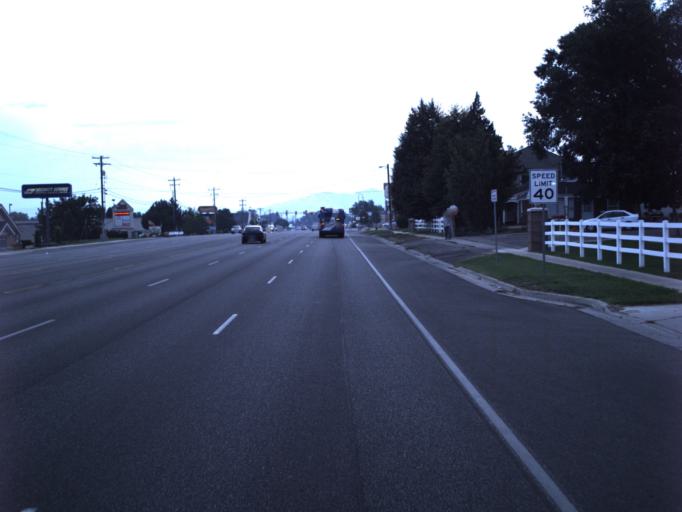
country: US
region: Utah
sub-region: Utah County
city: Pleasant Grove
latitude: 40.3533
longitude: -111.7333
